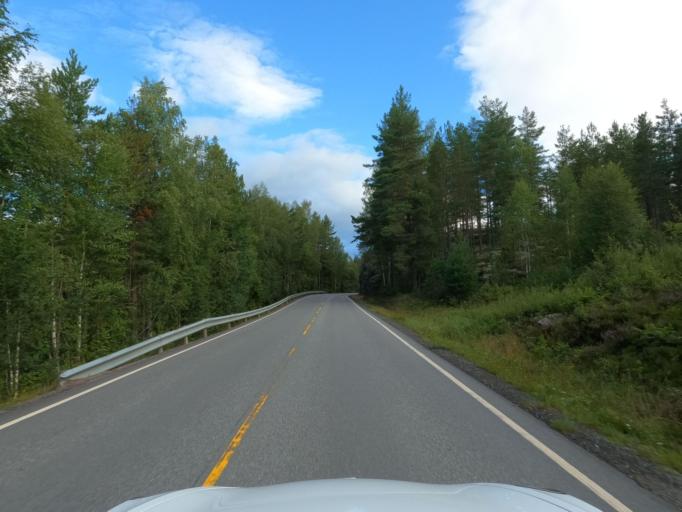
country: NO
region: Telemark
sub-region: Notodden
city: Notodden
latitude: 59.7316
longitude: 9.1590
